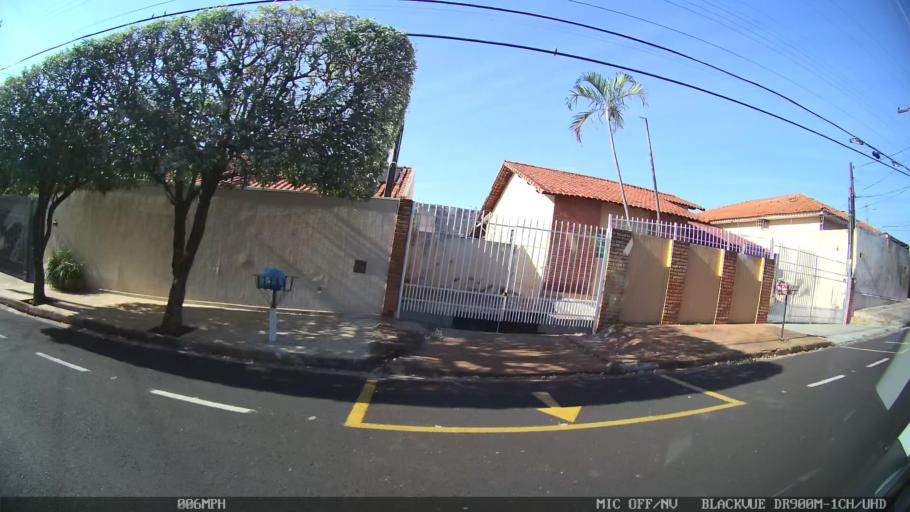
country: BR
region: Sao Paulo
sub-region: Sao Jose Do Rio Preto
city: Sao Jose do Rio Preto
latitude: -20.7803
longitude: -49.3565
